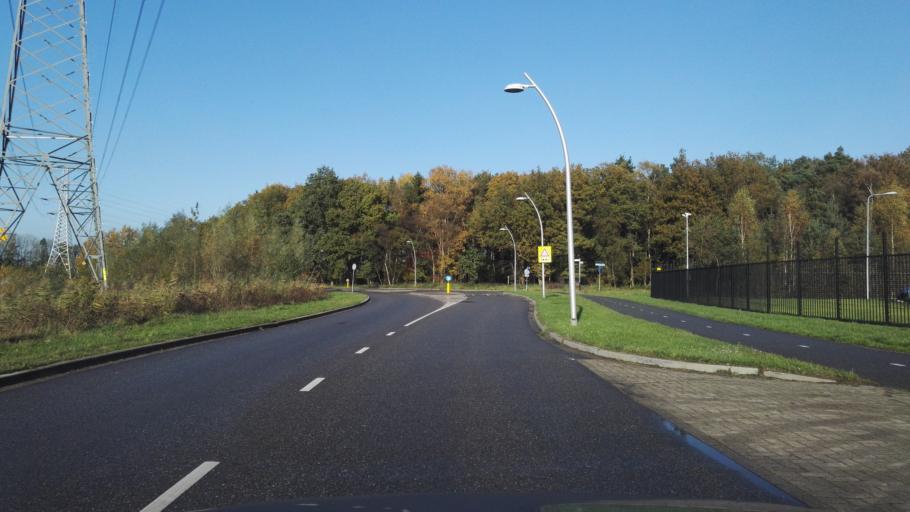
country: NL
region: Gelderland
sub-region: Gemeente Apeldoorn
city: Apeldoorn
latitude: 52.2001
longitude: 6.0249
